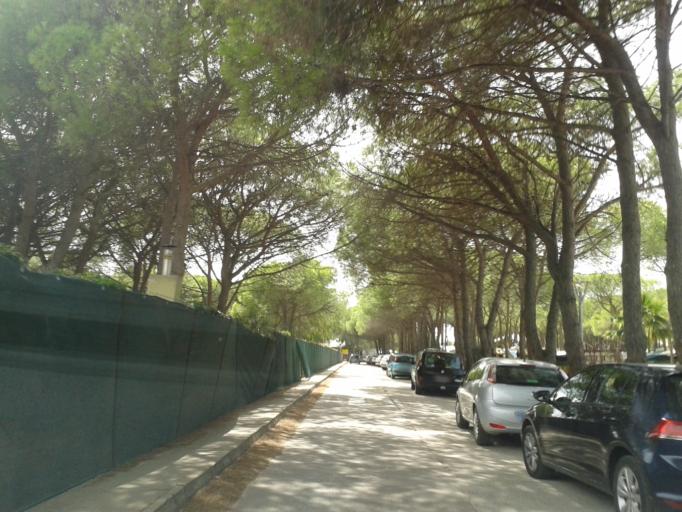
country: IT
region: Sardinia
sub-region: Provincia di Cagliari
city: Villasimius
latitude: 39.1230
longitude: 9.5125
